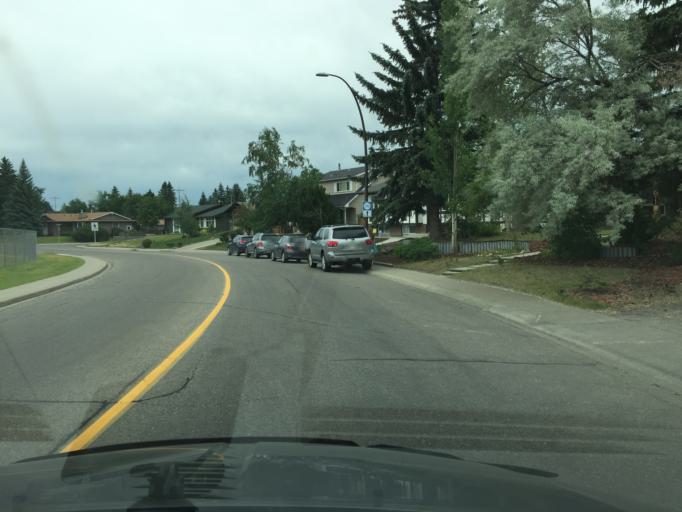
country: CA
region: Alberta
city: Calgary
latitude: 50.9415
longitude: -114.0439
